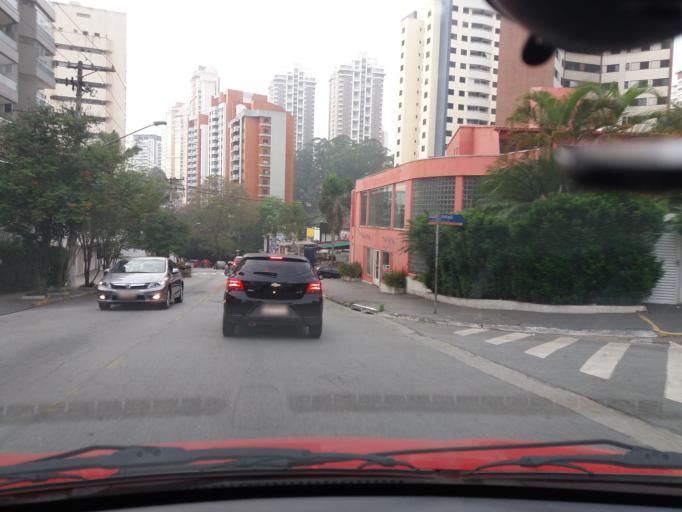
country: BR
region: Sao Paulo
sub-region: Taboao Da Serra
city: Taboao da Serra
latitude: -23.6285
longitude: -46.7322
